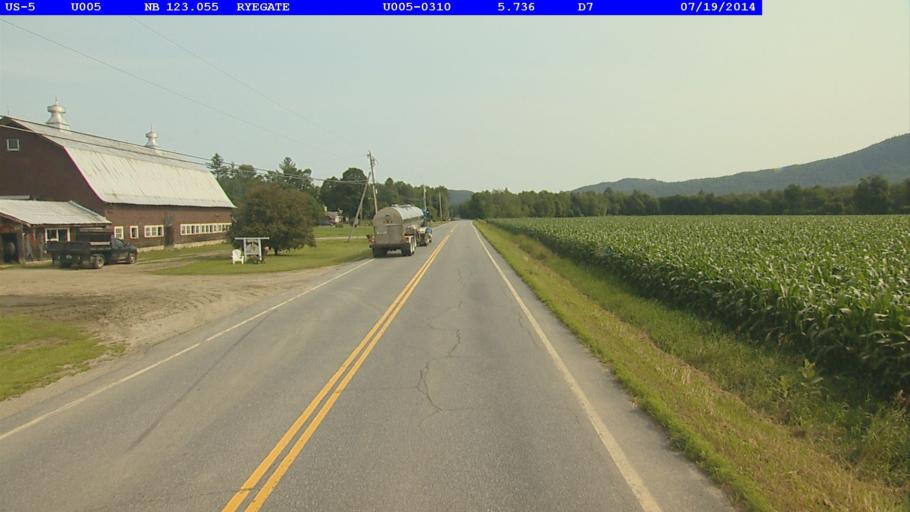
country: US
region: New Hampshire
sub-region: Grafton County
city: Woodsville
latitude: 44.2341
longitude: -72.0568
